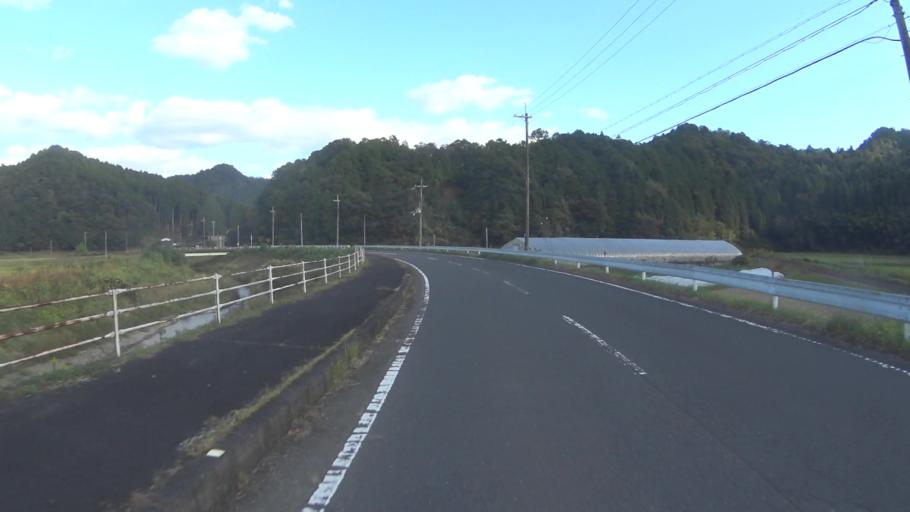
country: JP
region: Kyoto
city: Miyazu
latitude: 35.4383
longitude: 135.2186
